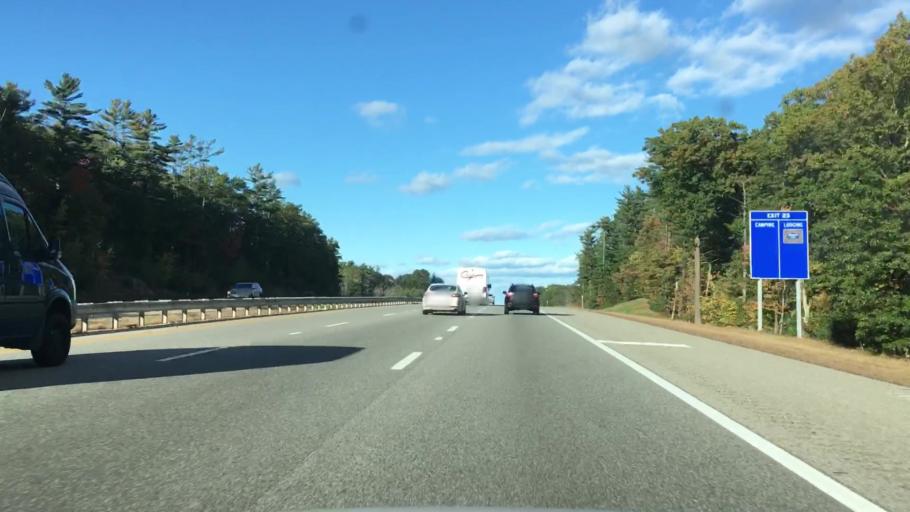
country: US
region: Maine
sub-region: York County
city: West Kennebunk
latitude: 43.3900
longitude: -70.5708
